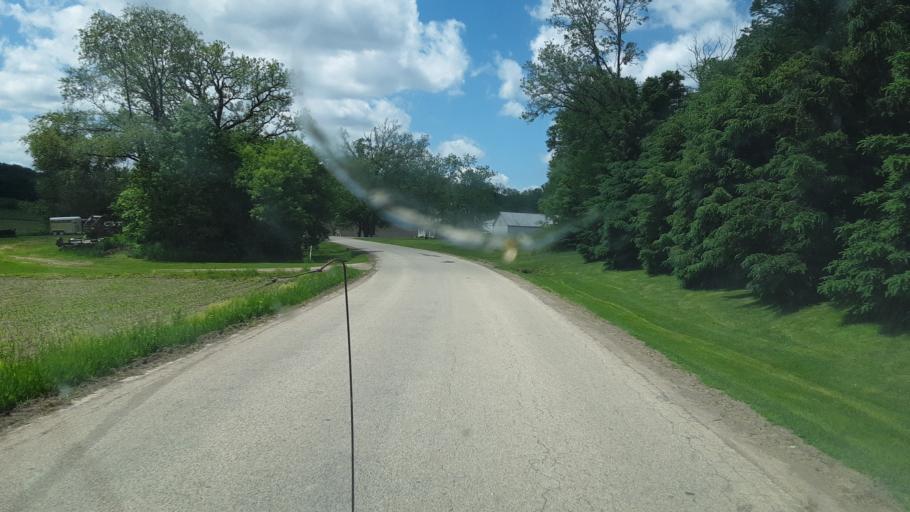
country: US
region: Wisconsin
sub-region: Sauk County
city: Reedsburg
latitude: 43.5765
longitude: -90.0037
